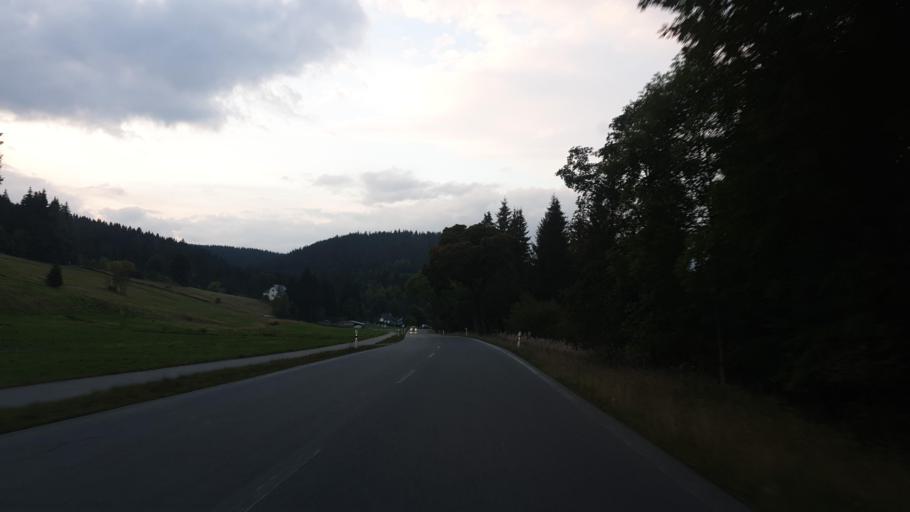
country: DE
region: Saxony
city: Sosa
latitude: 50.4443
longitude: 12.6350
